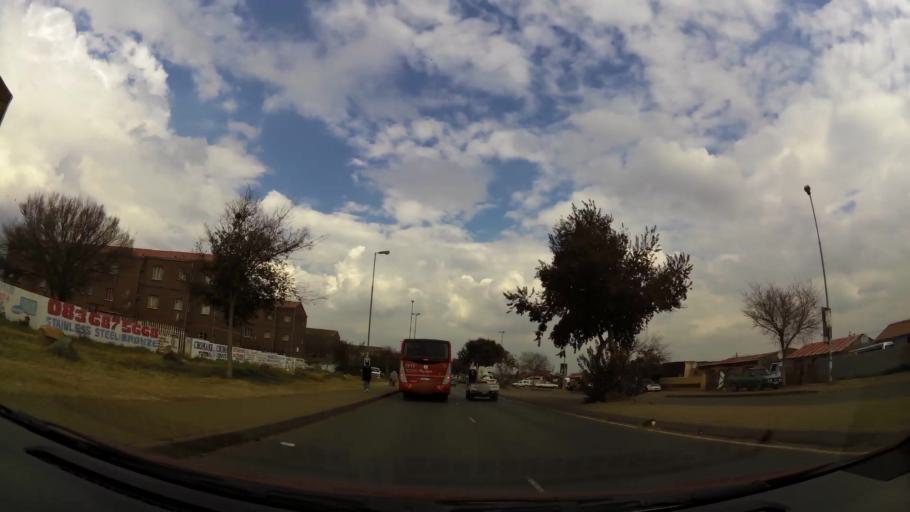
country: ZA
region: Gauteng
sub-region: City of Johannesburg Metropolitan Municipality
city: Soweto
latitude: -26.2538
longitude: 27.8546
